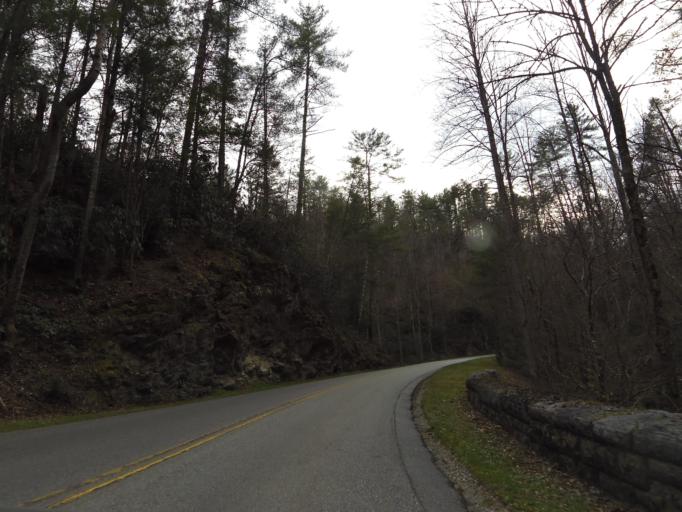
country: US
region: Tennessee
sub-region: Blount County
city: Wildwood
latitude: 35.6373
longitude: -83.7219
